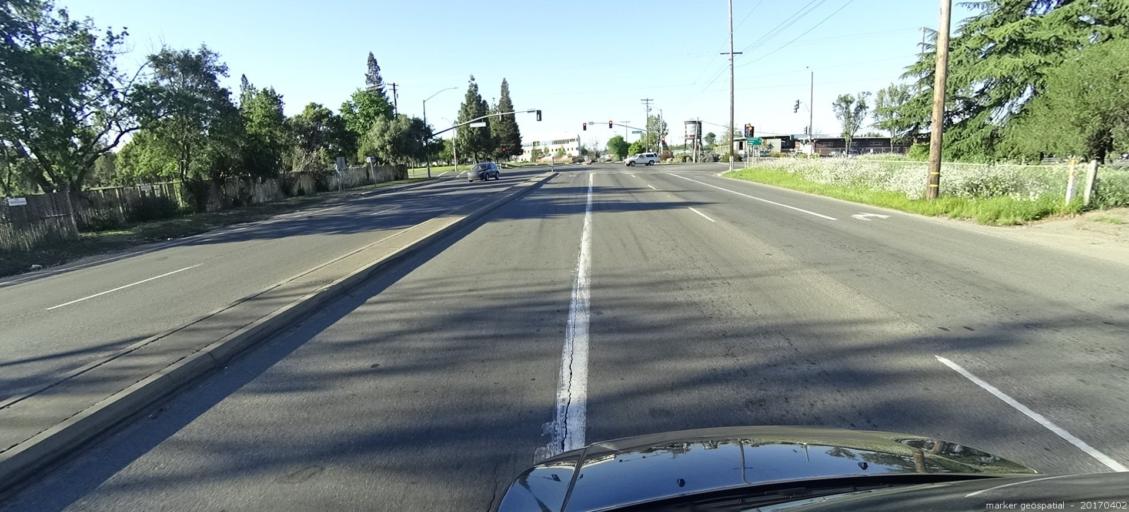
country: US
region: California
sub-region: Sacramento County
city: Rosemont
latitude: 38.5436
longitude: -121.3909
